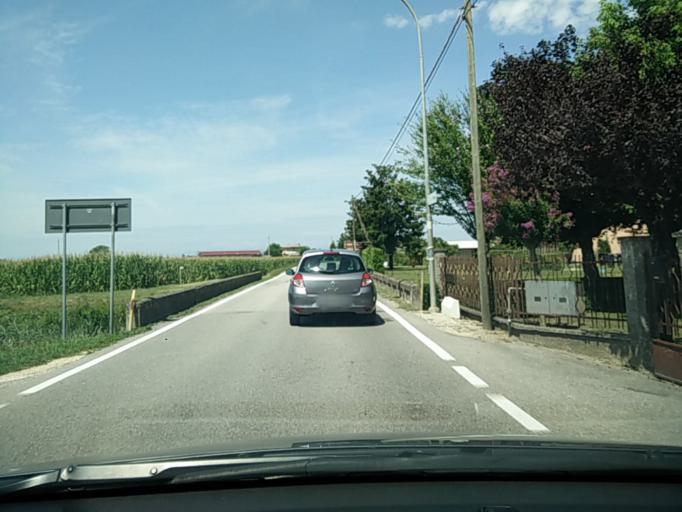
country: IT
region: Veneto
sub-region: Provincia di Venezia
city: Passarella
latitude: 45.5741
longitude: 12.6162
